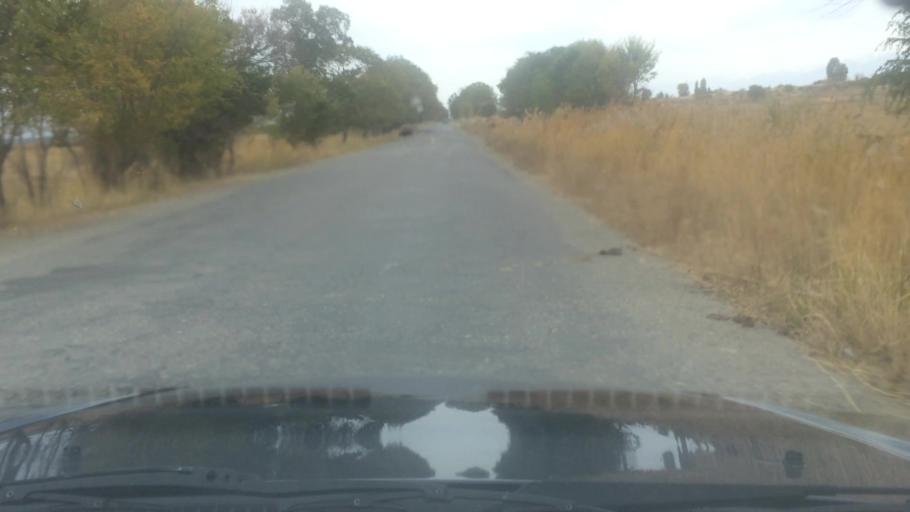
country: KG
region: Ysyk-Koel
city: Balykchy
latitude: 42.3066
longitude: 76.4688
